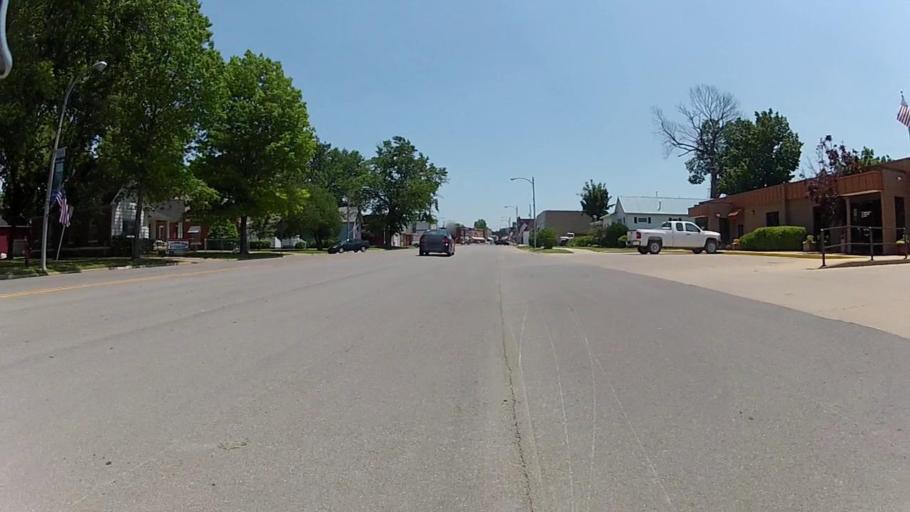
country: US
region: Kansas
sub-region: Montgomery County
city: Cherryvale
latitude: 37.2688
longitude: -95.5557
